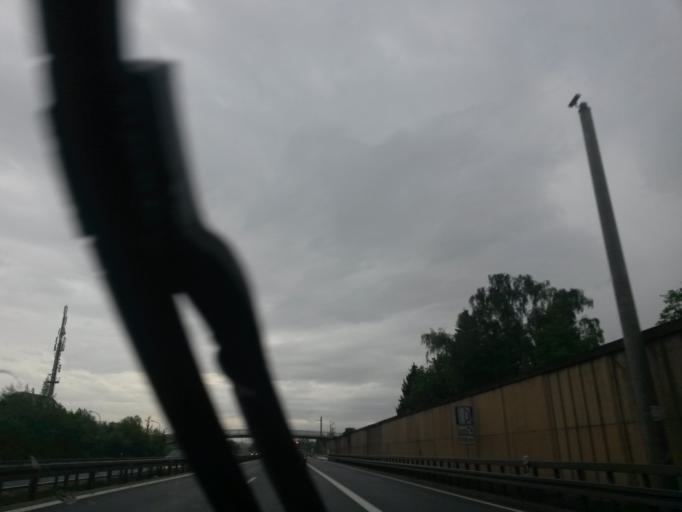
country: DE
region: Bavaria
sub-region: Regierungsbezirk Mittelfranken
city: Baiersdorf
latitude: 49.6570
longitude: 11.0360
